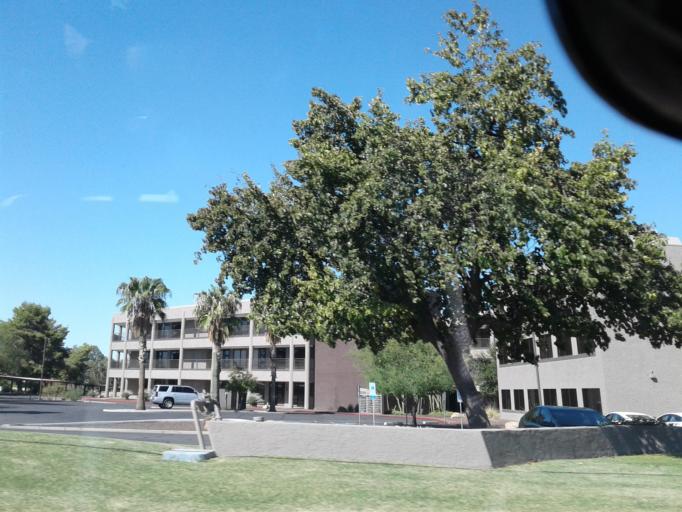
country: US
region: Arizona
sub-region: Maricopa County
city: Scottsdale
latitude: 33.4848
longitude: -111.9091
